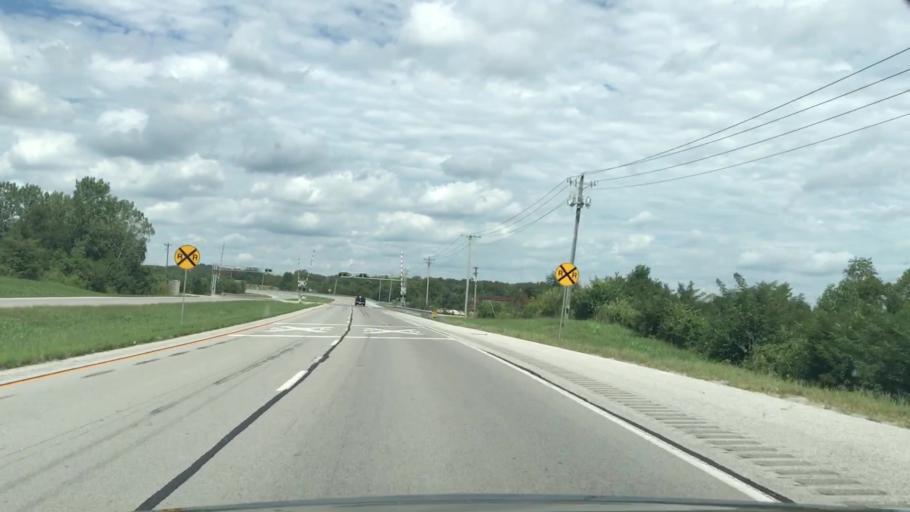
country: US
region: Kentucky
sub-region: Logan County
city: Russellville
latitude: 36.8611
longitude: -86.8632
